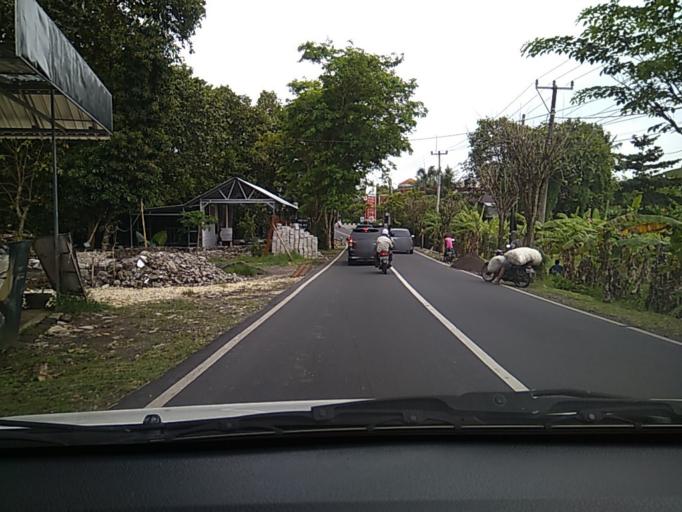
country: ID
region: Bali
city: Banjar Kerobokan
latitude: -8.6302
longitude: 115.1324
